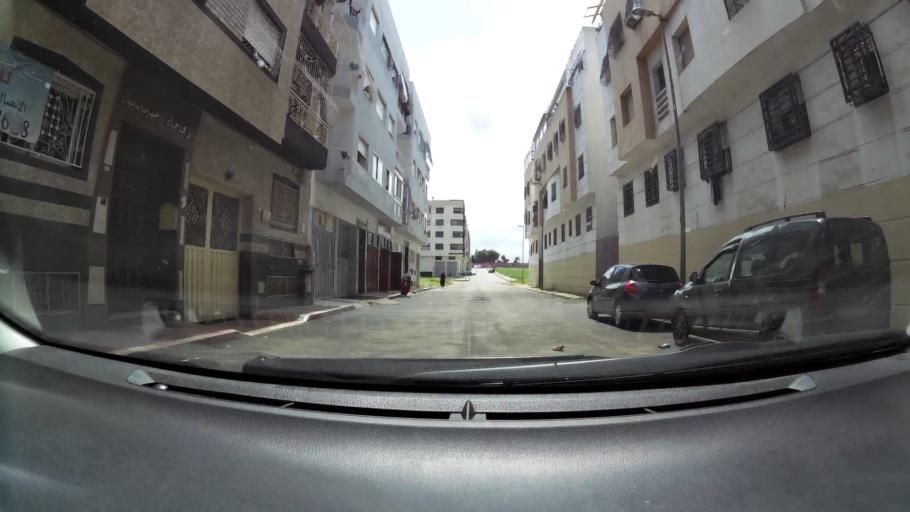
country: MA
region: Grand Casablanca
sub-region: Casablanca
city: Casablanca
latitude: 33.5421
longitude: -7.5628
